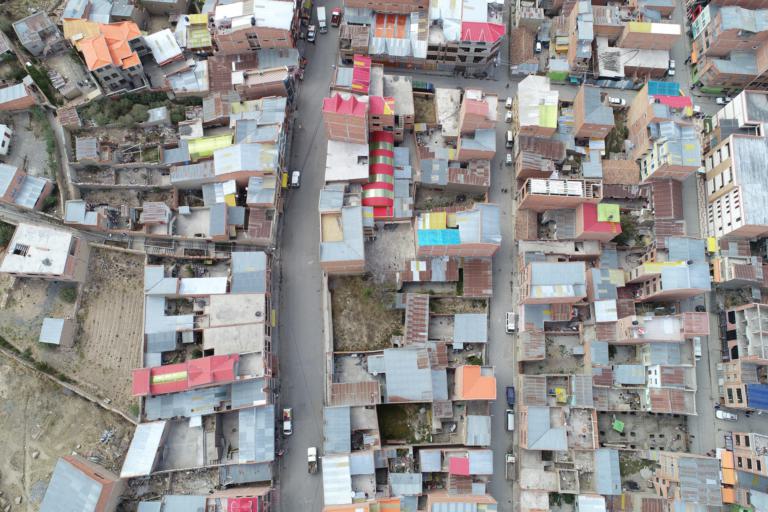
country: BO
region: La Paz
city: Achacachi
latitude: -16.0418
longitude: -68.6847
